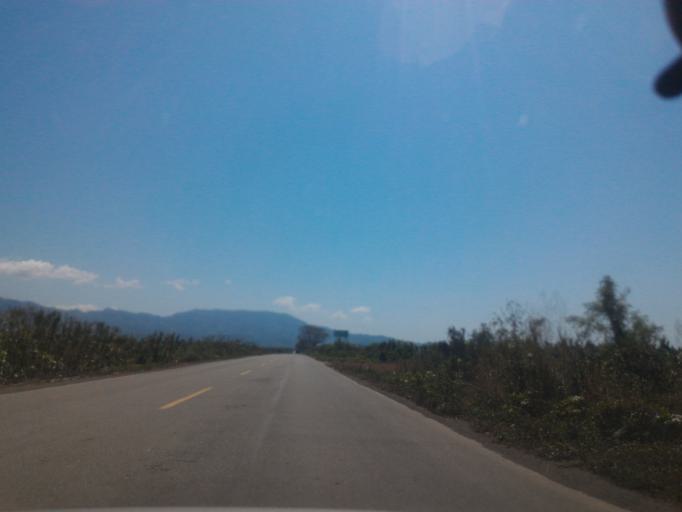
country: MX
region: Michoacan
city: Coahuayana Viejo
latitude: 18.7069
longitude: -103.7081
